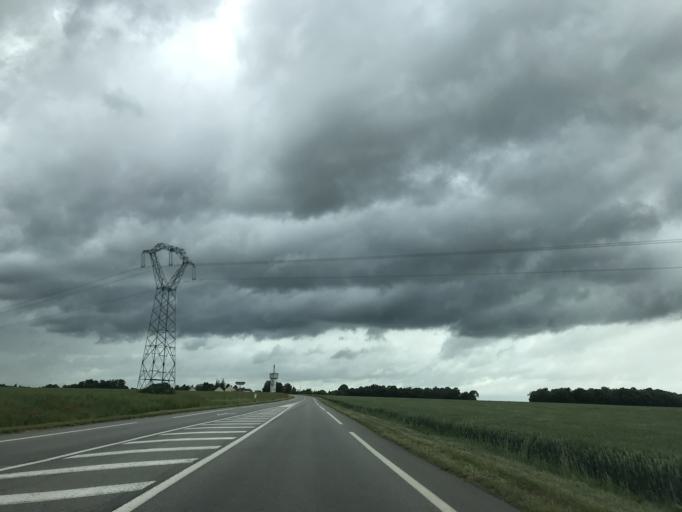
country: FR
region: Haute-Normandie
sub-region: Departement de l'Eure
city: La Couture-Boussey
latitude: 48.8946
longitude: 1.4212
